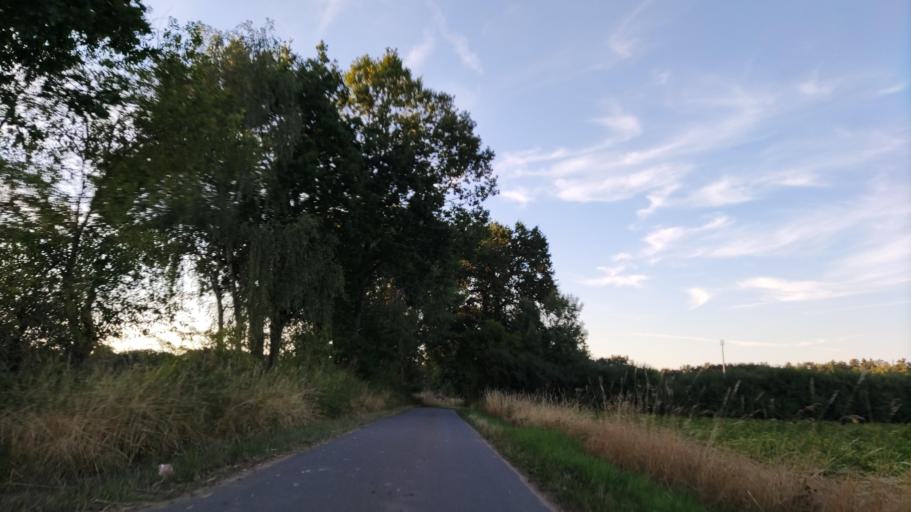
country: DE
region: Lower Saxony
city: Vastorf
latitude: 53.1999
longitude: 10.5327
